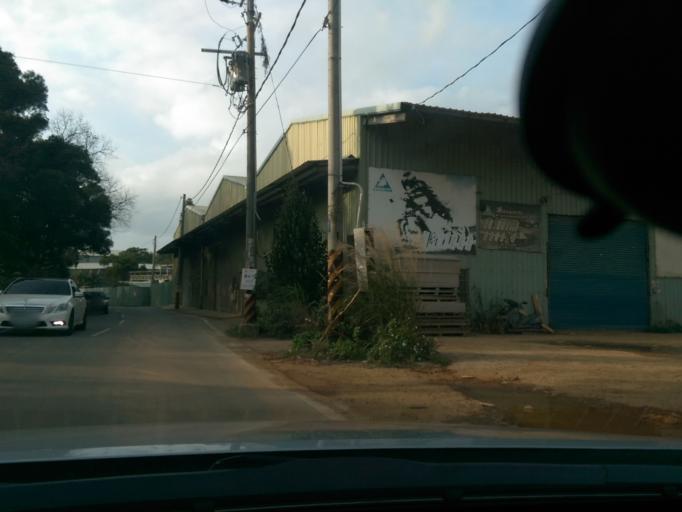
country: TW
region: Taiwan
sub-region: Taoyuan
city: Taoyuan
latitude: 25.0876
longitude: 121.3726
